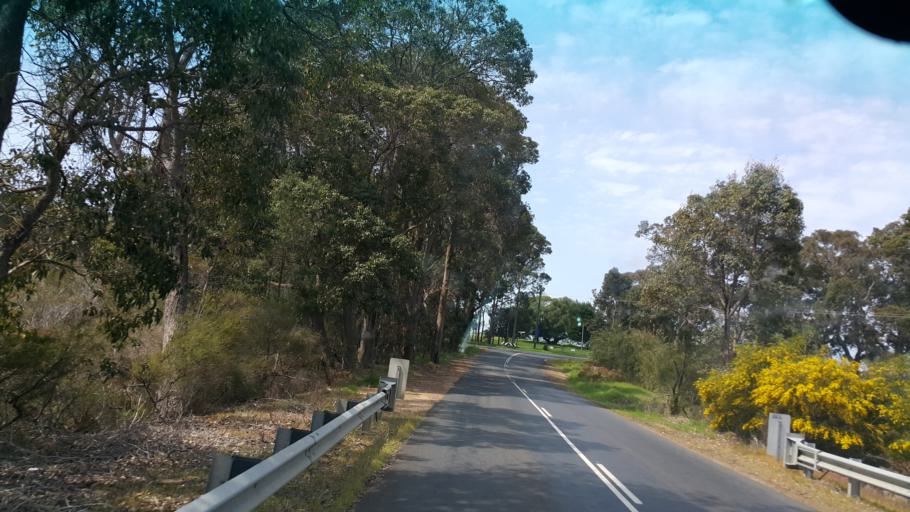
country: AU
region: Western Australia
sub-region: Busselton
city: Vasse
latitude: -33.7483
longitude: 115.1901
